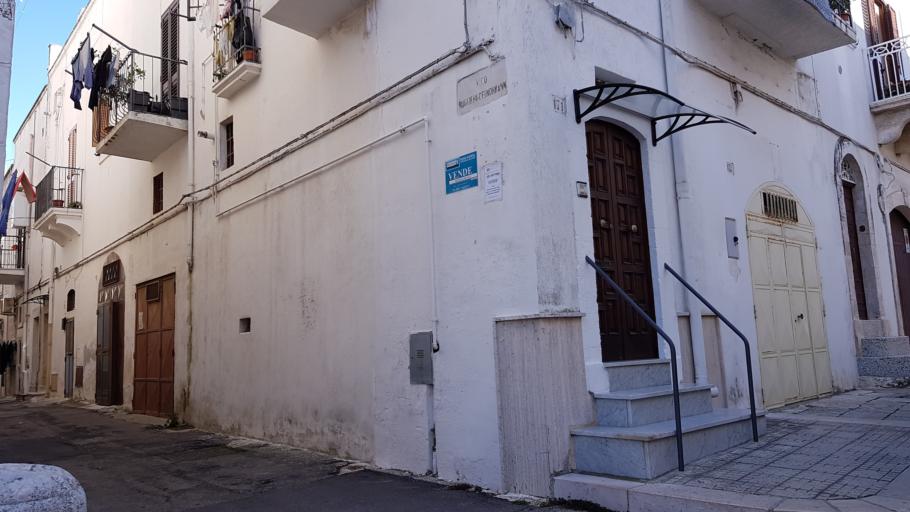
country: IT
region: Apulia
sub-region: Provincia di Brindisi
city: Ostuni
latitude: 40.7277
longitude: 17.5806
